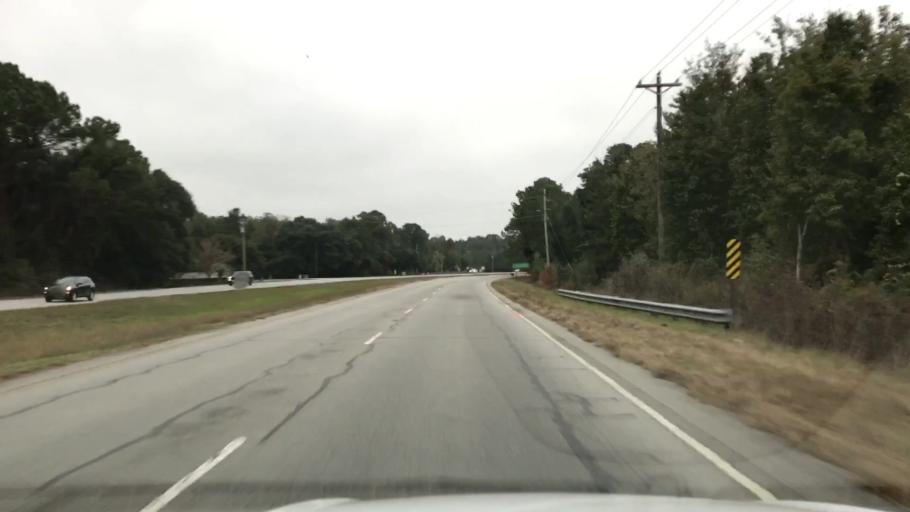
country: US
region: South Carolina
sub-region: Charleston County
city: Awendaw
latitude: 33.0761
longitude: -79.5108
